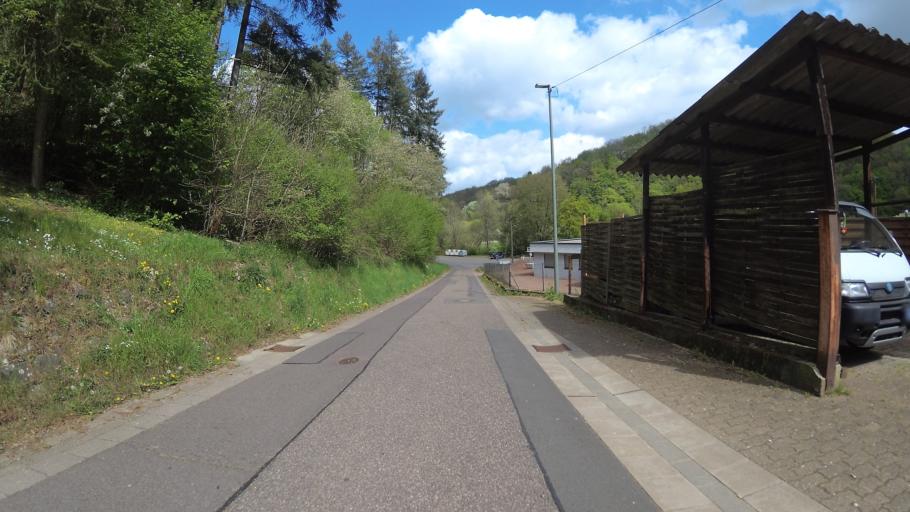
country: DE
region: Saarland
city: Schmelz
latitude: 49.4882
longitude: 6.8542
